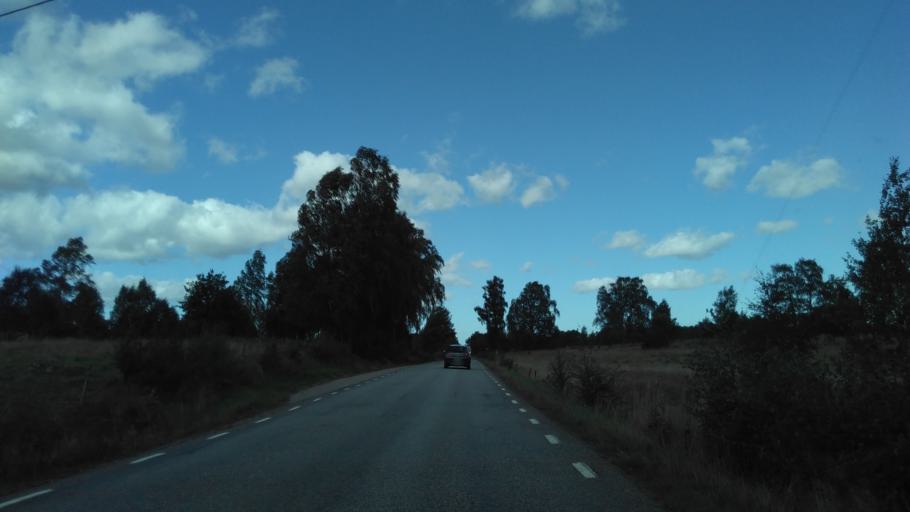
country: SE
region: Vaestra Goetaland
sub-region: Herrljunga Kommun
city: Herrljunga
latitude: 58.1477
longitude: 13.0197
